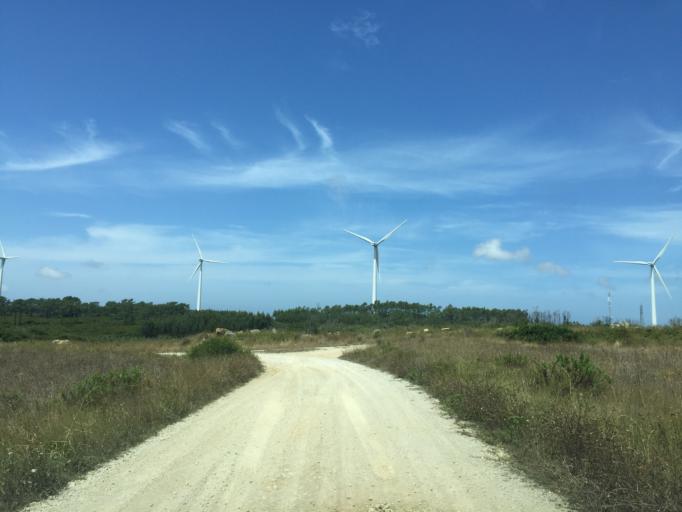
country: PT
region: Leiria
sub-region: Peniche
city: Atouguia da Baleia
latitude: 39.3174
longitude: -9.2591
